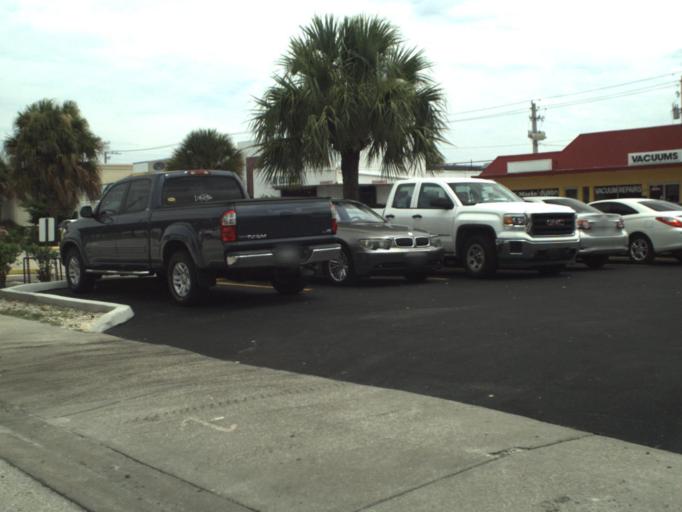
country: US
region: Florida
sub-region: Palm Beach County
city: Lake Park
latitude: 26.8058
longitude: -80.0555
